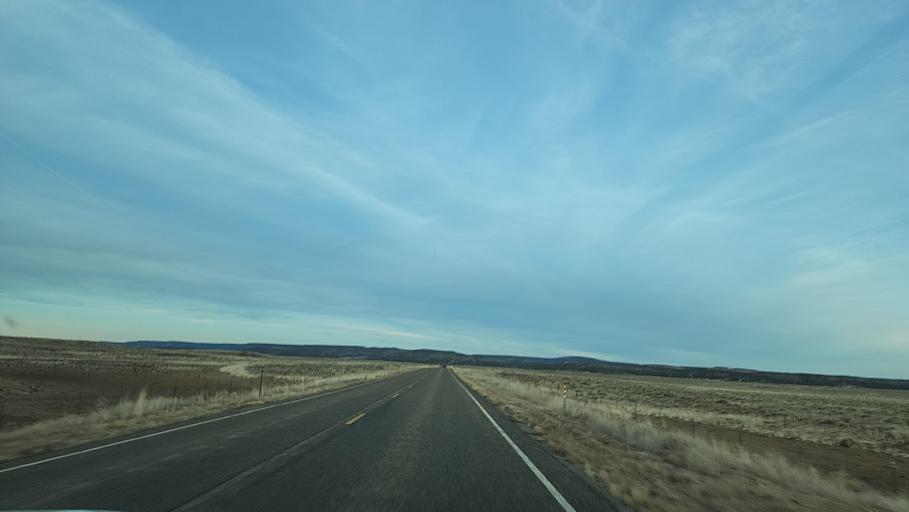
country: US
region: New Mexico
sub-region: Cibola County
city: Grants
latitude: 34.7001
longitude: -108.0373
